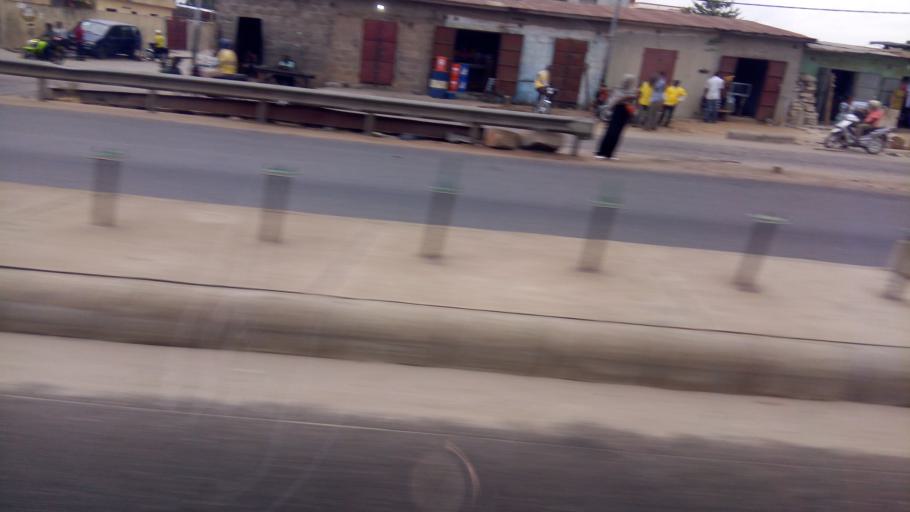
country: BJ
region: Atlantique
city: Abomey-Calavi
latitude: 6.3916
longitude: 2.3503
